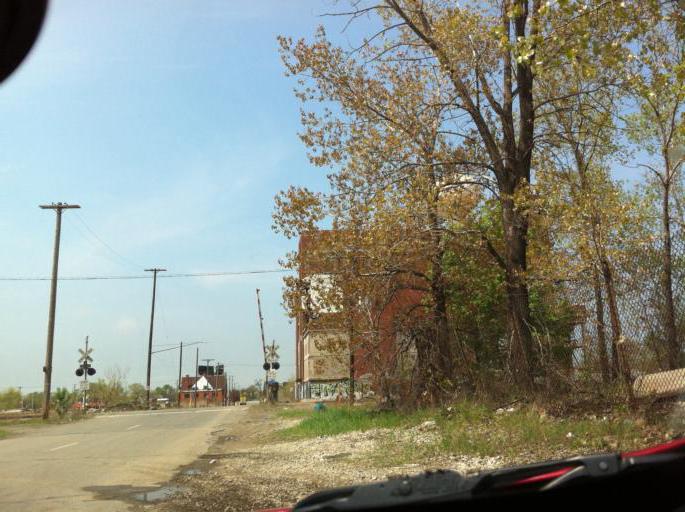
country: US
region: Michigan
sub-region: Wayne County
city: River Rouge
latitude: 42.3044
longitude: -83.1001
